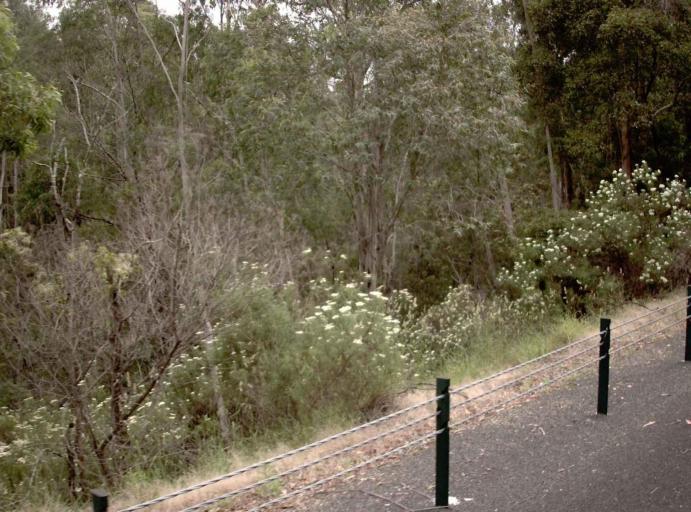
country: AU
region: New South Wales
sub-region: Bombala
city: Bombala
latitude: -37.2671
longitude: 149.2290
